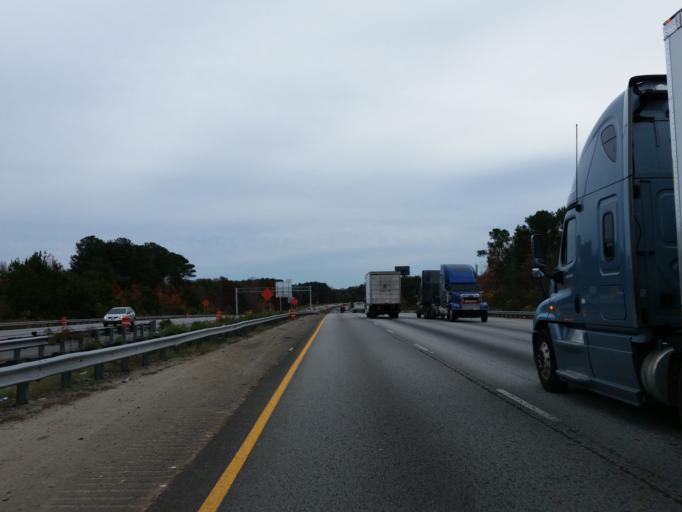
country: US
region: Georgia
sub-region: Henry County
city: McDonough
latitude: 33.4108
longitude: -84.1608
